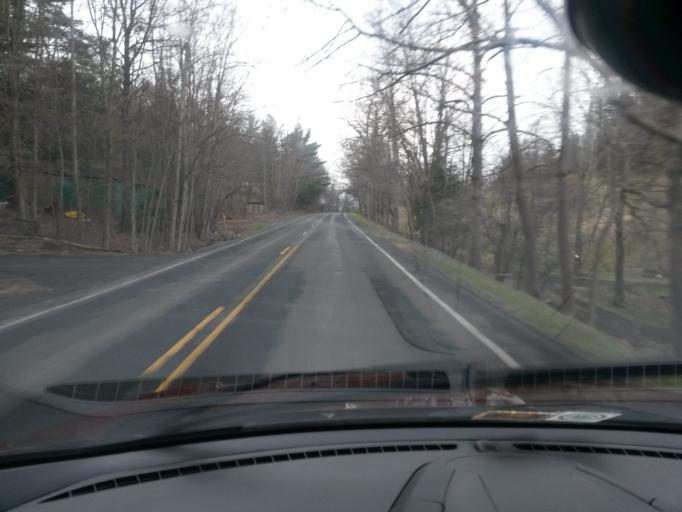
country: US
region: Virginia
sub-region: Bath County
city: Warm Springs
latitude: 38.1269
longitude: -79.7509
